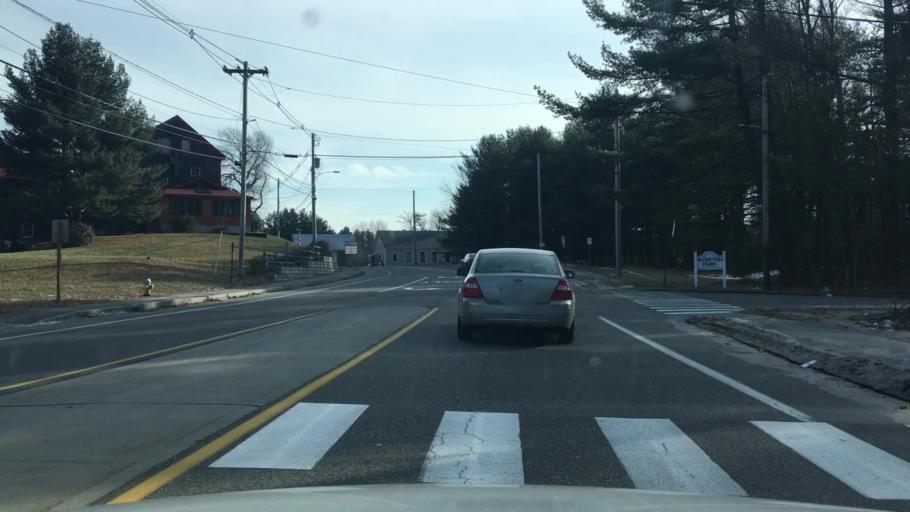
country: US
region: Maine
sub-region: Cumberland County
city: Westbrook
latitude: 43.7006
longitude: -70.3205
